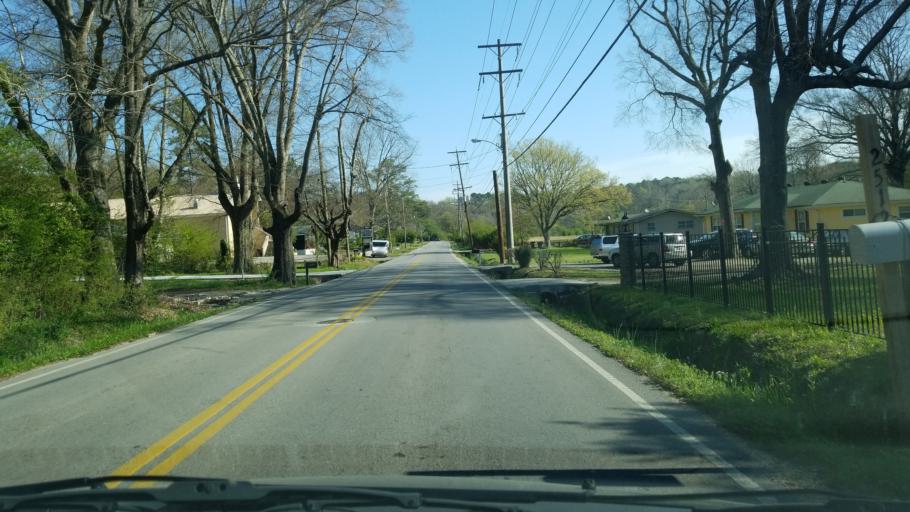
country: US
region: Tennessee
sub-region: Hamilton County
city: East Chattanooga
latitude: 35.0613
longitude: -85.2291
